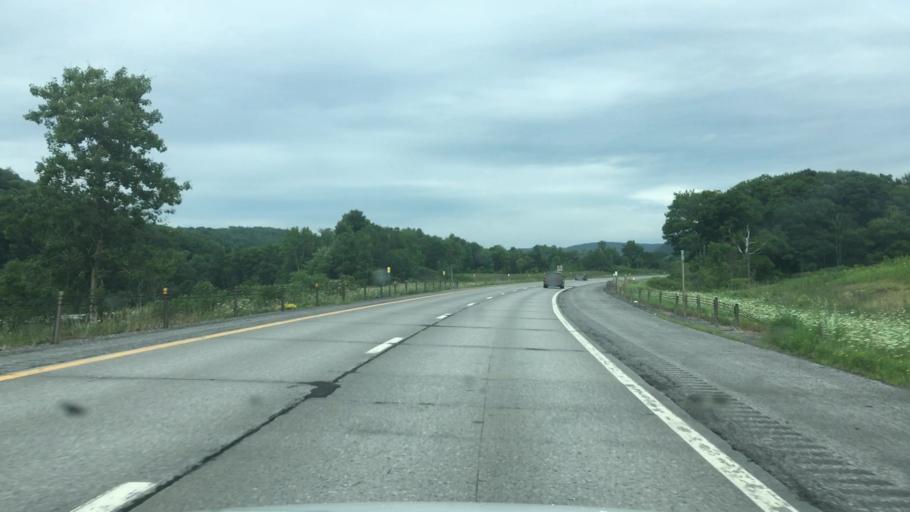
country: US
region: New York
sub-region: Otsego County
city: Worcester
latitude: 42.6041
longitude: -74.6966
